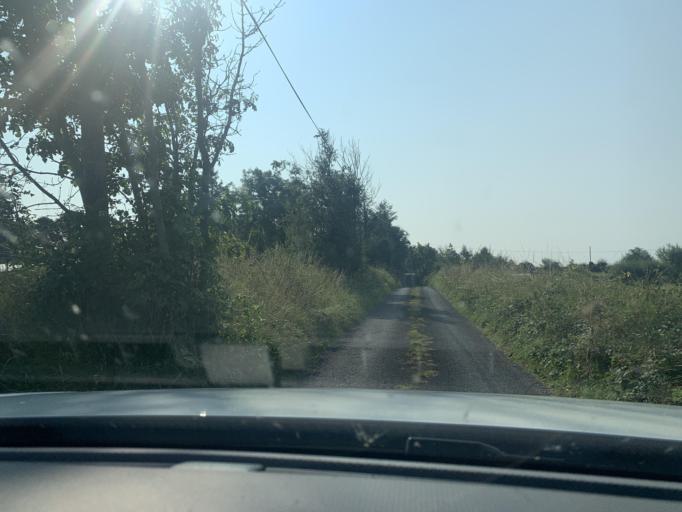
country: IE
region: Connaught
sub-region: Maigh Eo
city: Ballyhaunis
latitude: 53.7917
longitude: -8.7401
